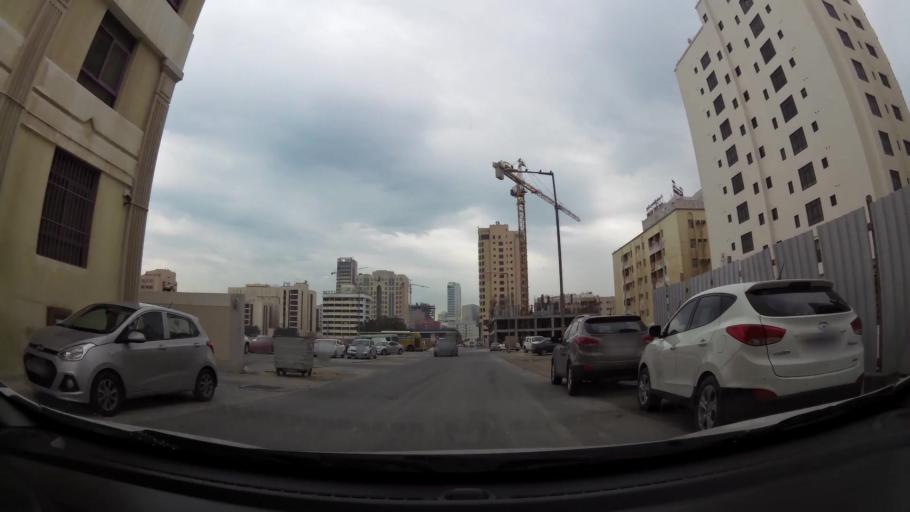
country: BH
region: Manama
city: Manama
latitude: 26.2387
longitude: 50.5924
